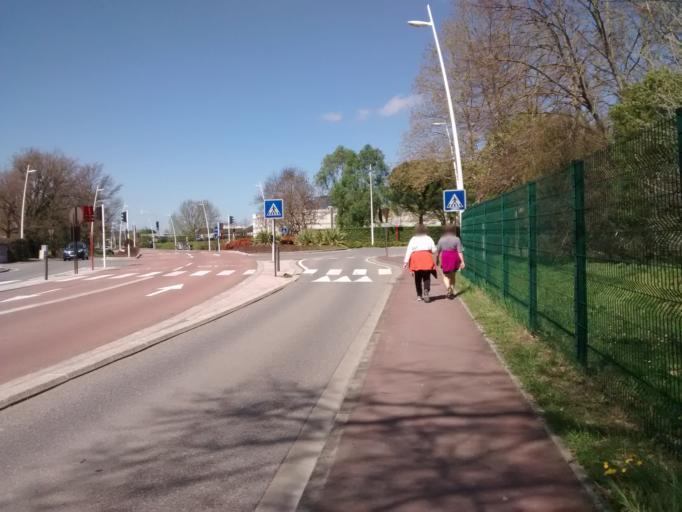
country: FR
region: Midi-Pyrenees
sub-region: Departement de la Haute-Garonne
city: Labege
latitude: 43.5383
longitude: 1.5163
